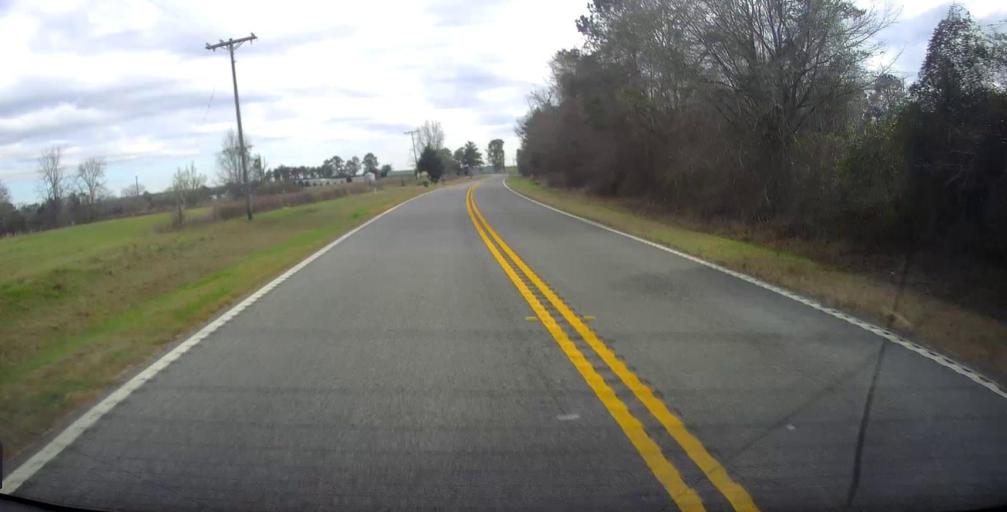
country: US
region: Georgia
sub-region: Marion County
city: Buena Vista
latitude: 32.4477
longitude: -84.4408
